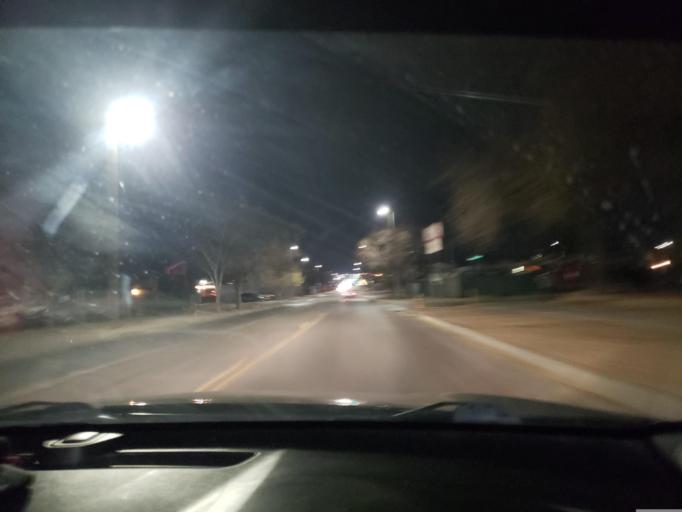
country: US
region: New Mexico
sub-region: Bernalillo County
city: Albuquerque
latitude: 35.0744
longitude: -106.6221
